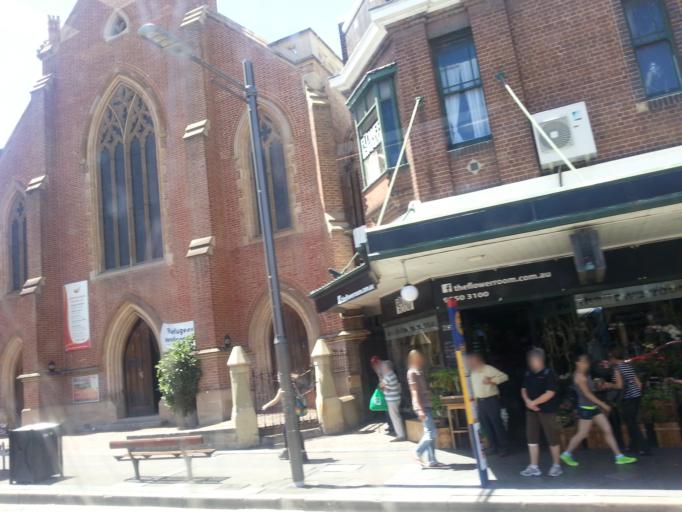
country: AU
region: New South Wales
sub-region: Marrickville
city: Newtown
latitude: -33.8963
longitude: 151.1803
